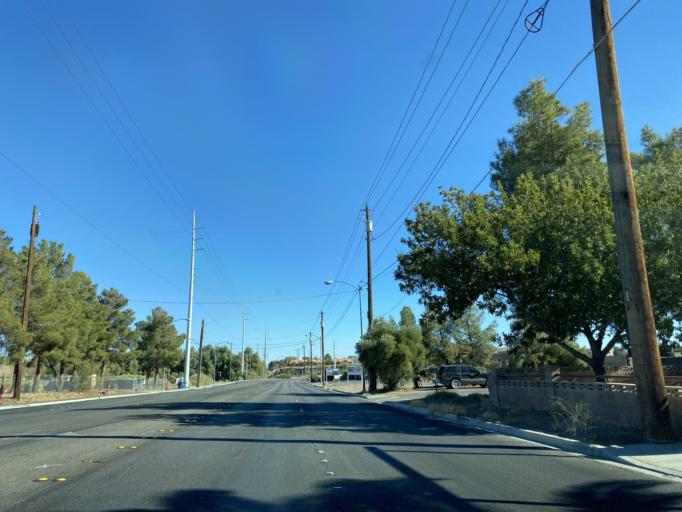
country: US
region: Nevada
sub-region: Clark County
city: Whitney
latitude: 36.0784
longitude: -115.0866
